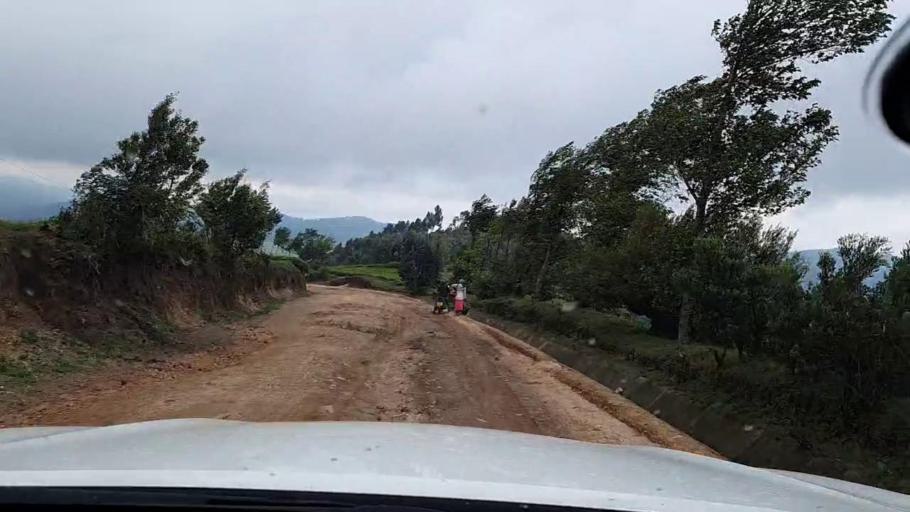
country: RW
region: Western Province
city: Kibuye
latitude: -2.2442
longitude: 29.3463
